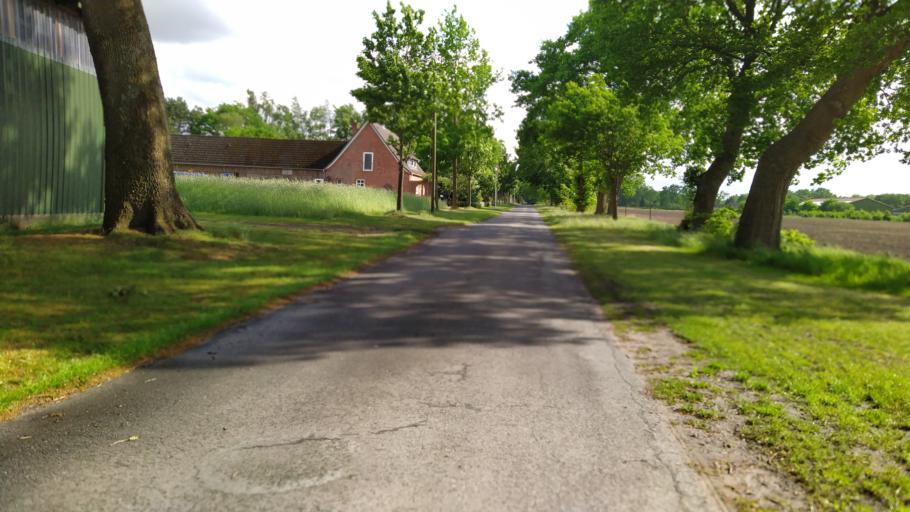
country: DE
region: Lower Saxony
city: Brest
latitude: 53.4559
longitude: 9.3920
